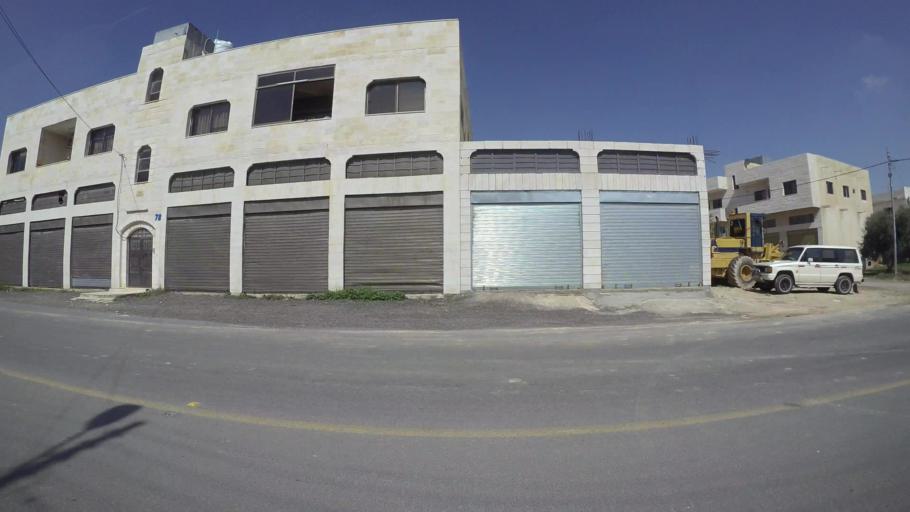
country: JO
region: Amman
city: Al Bunayyat ash Shamaliyah
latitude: 31.8981
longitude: 35.9023
